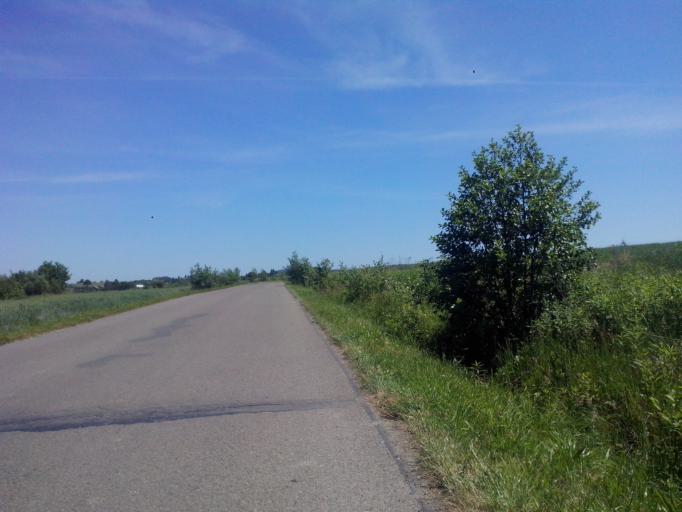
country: PL
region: Subcarpathian Voivodeship
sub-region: Powiat strzyzowski
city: Wisniowa
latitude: 49.8562
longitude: 21.6923
